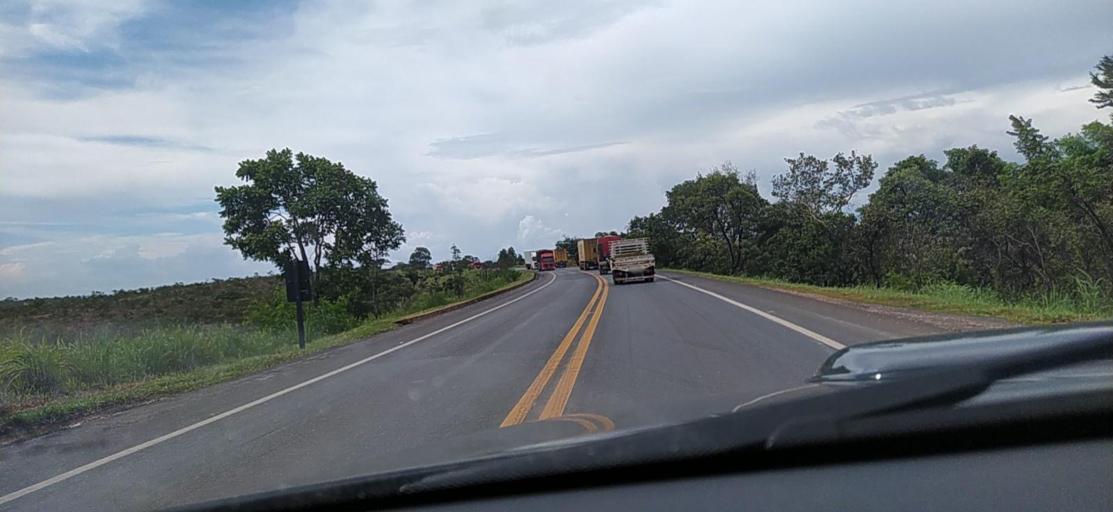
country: BR
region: Minas Gerais
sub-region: Montes Claros
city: Montes Claros
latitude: -16.8373
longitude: -43.8491
